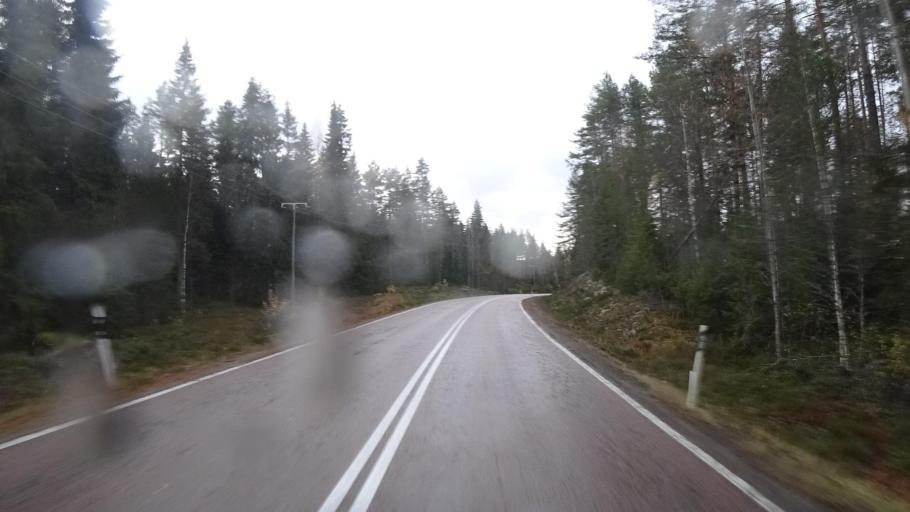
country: FI
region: Southern Savonia
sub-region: Mikkeli
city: Kangasniemi
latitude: 62.0774
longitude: 26.6927
